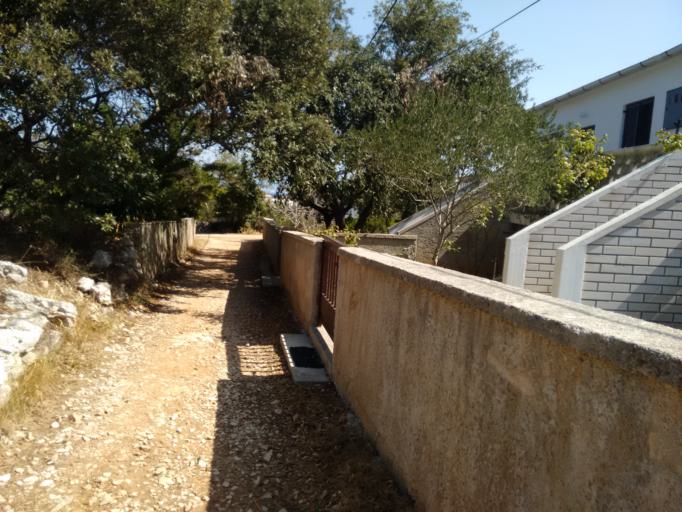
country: HR
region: Licko-Senjska
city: Novalja
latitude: 44.3731
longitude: 14.7001
